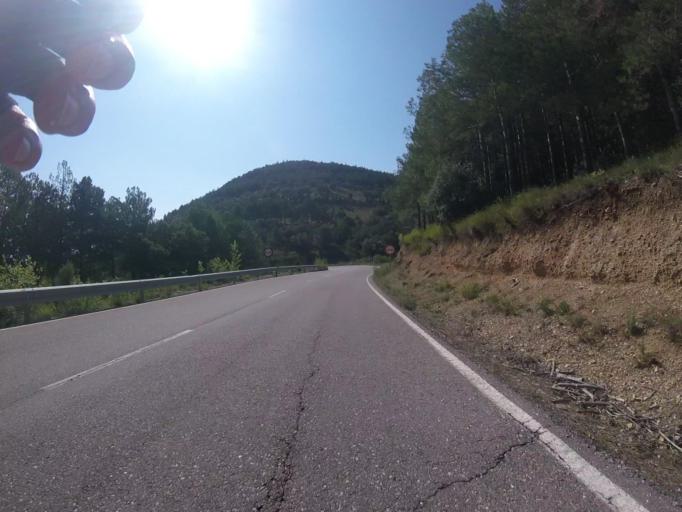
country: ES
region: Valencia
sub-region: Provincia de Castello
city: Benafigos
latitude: 40.2678
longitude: -0.2444
